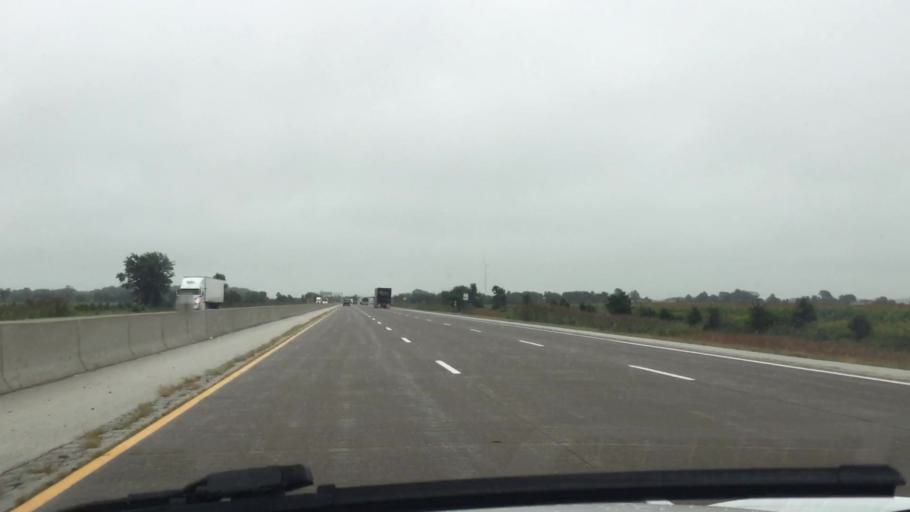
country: US
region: Michigan
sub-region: Wayne County
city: Grosse Pointe Farms
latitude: 42.2365
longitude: -82.7024
